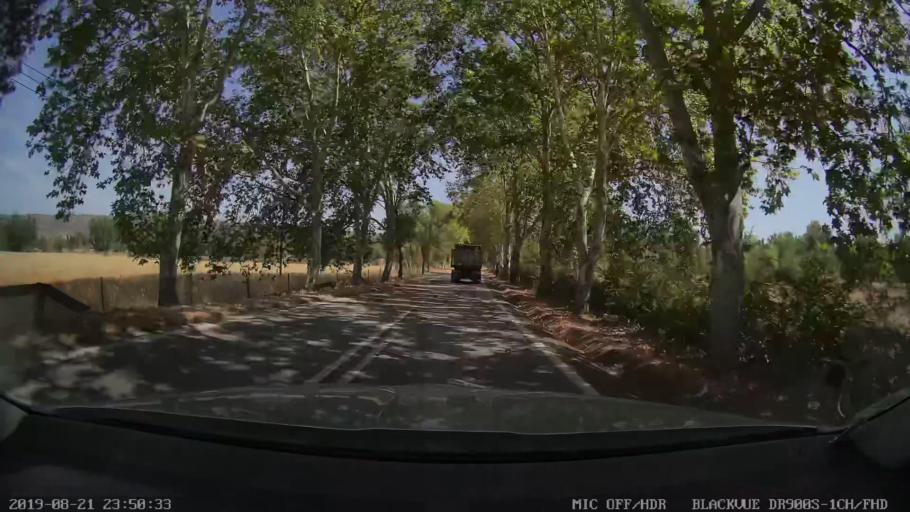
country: PT
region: Castelo Branco
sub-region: Idanha-A-Nova
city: Idanha-a-Nova
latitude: 39.8916
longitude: -7.2417
